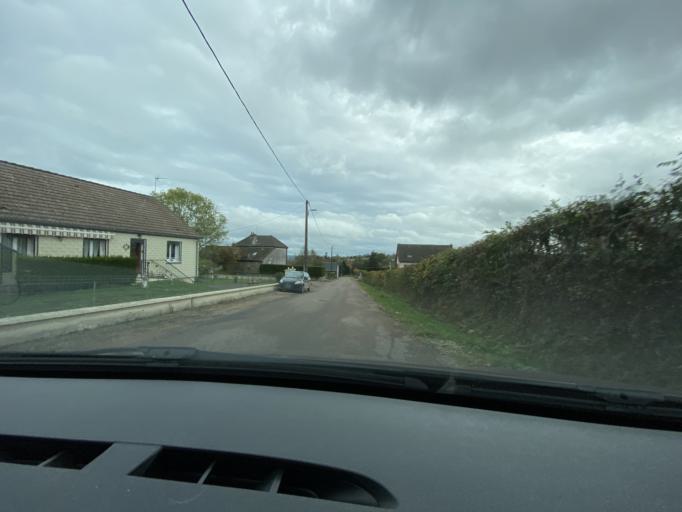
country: FR
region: Bourgogne
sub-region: Departement de la Cote-d'Or
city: Saulieu
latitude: 47.2810
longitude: 4.2193
